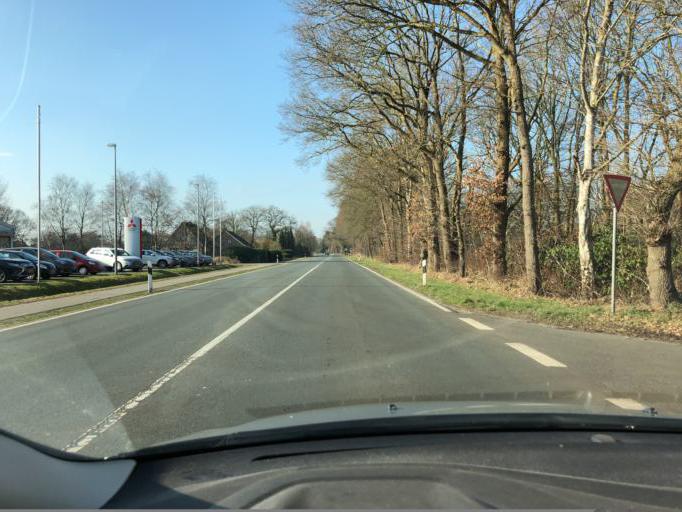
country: DE
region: Lower Saxony
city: Schwerinsdorf
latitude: 53.3030
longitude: 7.7361
